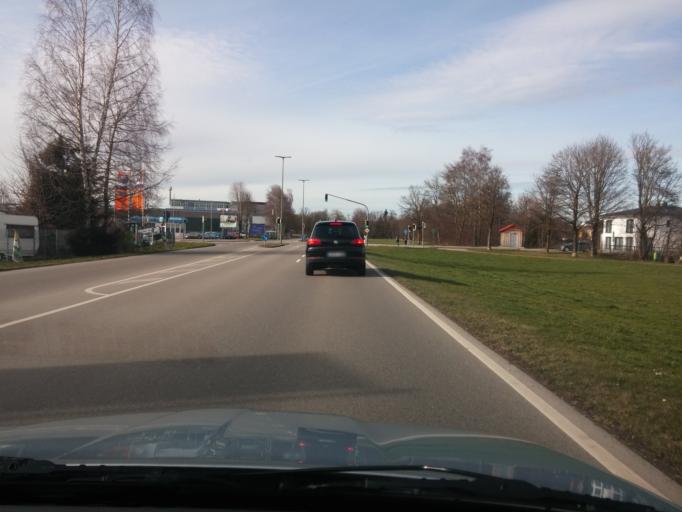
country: DE
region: Bavaria
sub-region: Swabia
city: Memmingen
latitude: 47.9881
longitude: 10.2022
